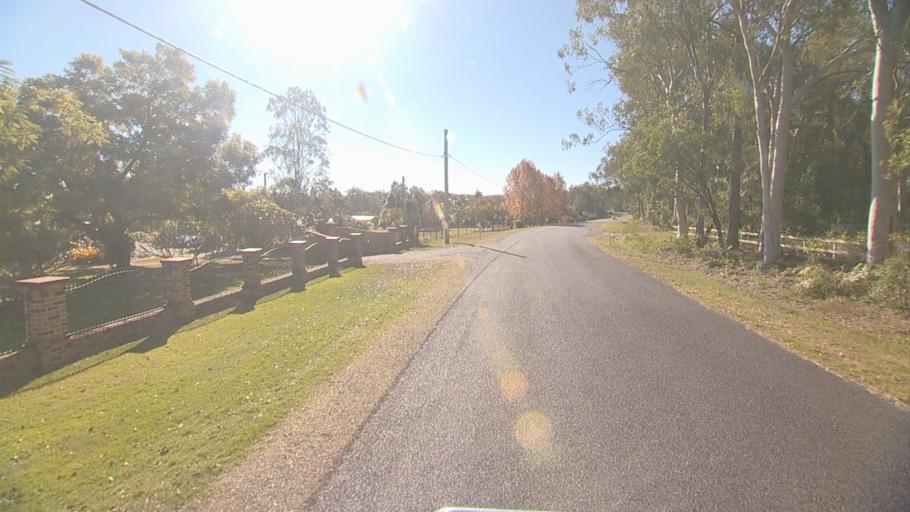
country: AU
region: Queensland
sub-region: Logan
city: Chambers Flat
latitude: -27.7382
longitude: 153.0778
